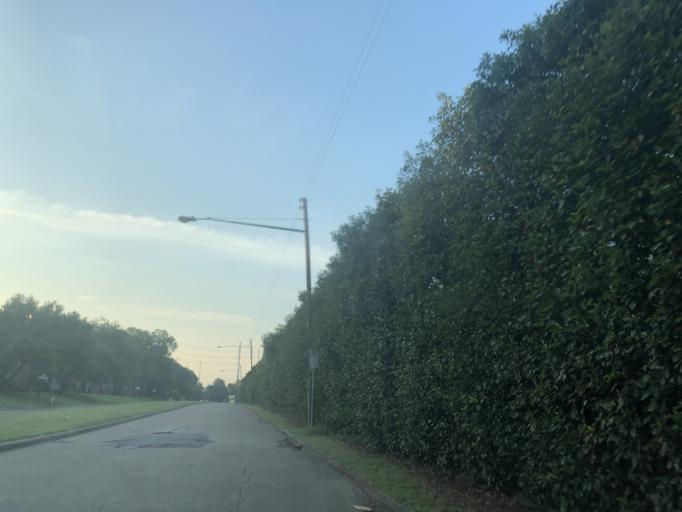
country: US
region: Texas
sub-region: Dallas County
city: Garland
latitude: 32.8456
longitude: -96.6389
